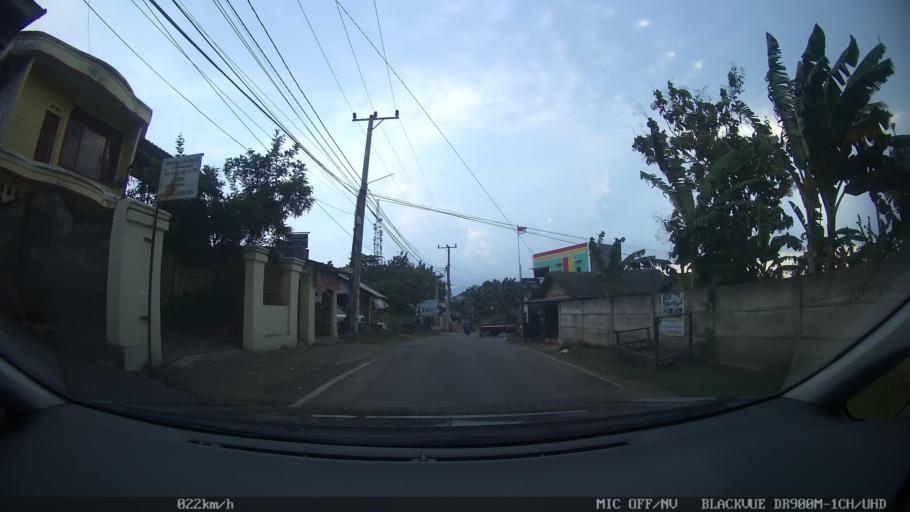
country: ID
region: Lampung
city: Kedaton
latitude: -5.3506
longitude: 105.2409
